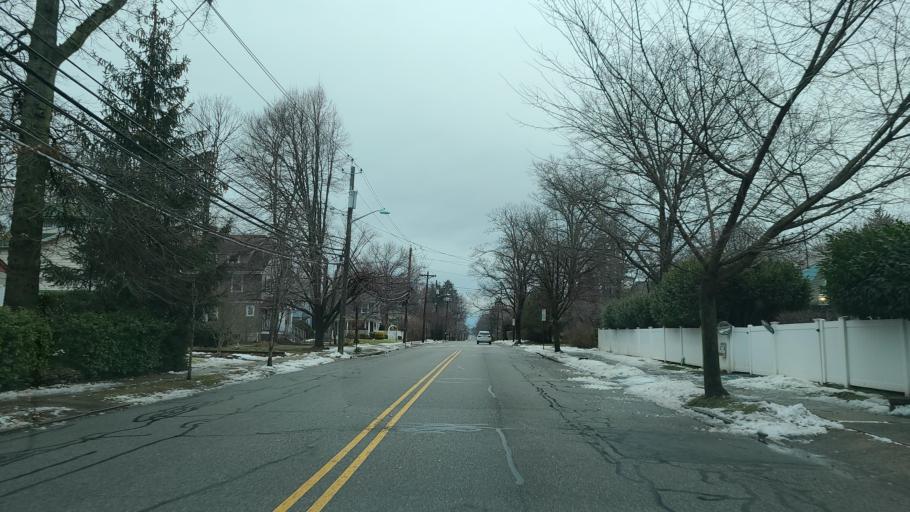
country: US
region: New Jersey
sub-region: Essex County
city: Upper Montclair
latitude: 40.8494
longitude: -74.2034
